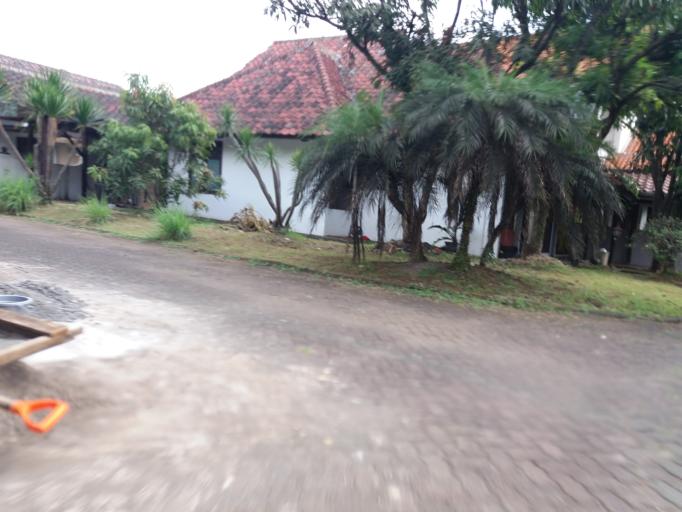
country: ID
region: West Java
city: Bandung
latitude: -6.9189
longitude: 107.6536
